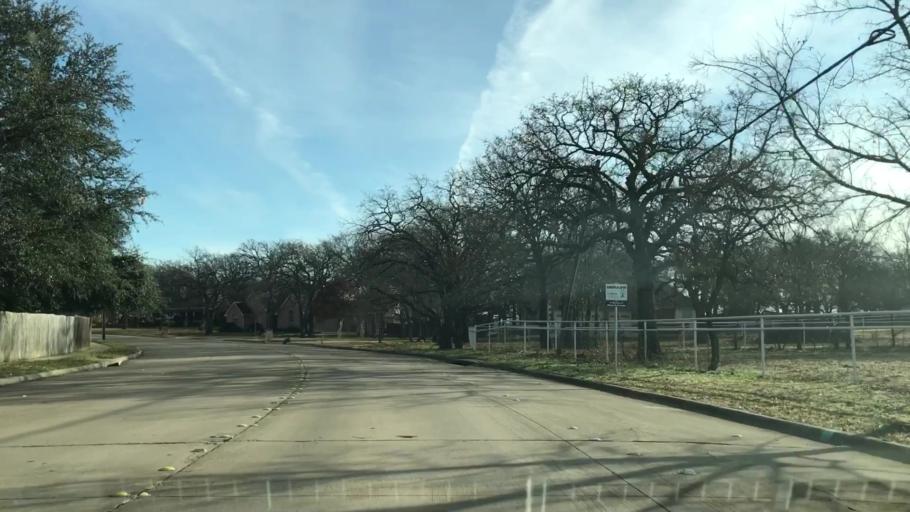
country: US
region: Texas
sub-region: Tarrant County
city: Watauga
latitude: 32.8749
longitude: -97.2199
